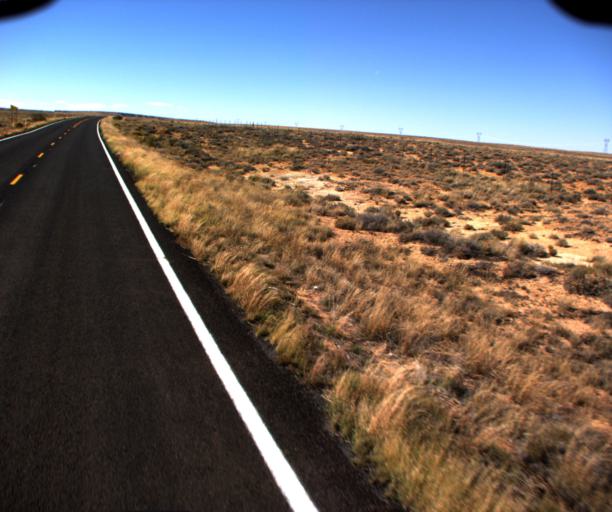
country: US
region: Arizona
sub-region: Navajo County
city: First Mesa
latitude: 35.9697
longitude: -110.7982
